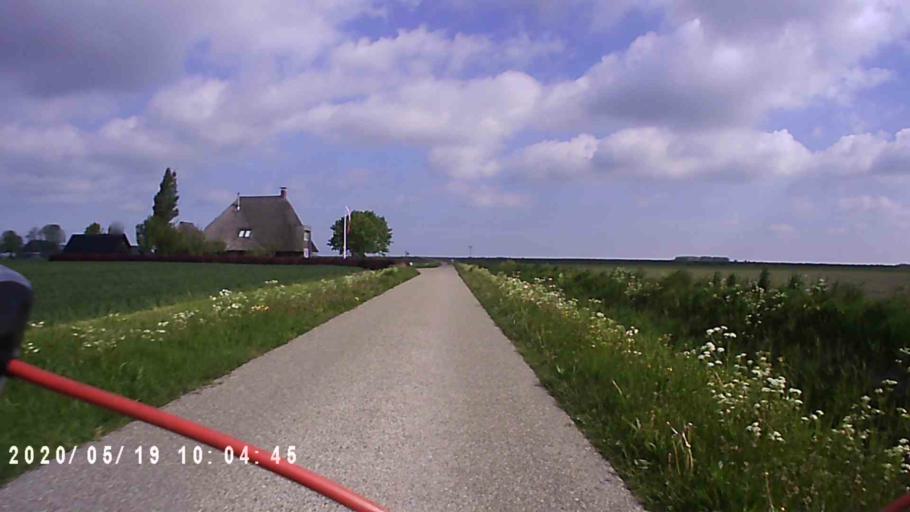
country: NL
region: Friesland
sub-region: Gemeente Kollumerland en Nieuwkruisland
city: Kollum
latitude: 53.3071
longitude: 6.2279
